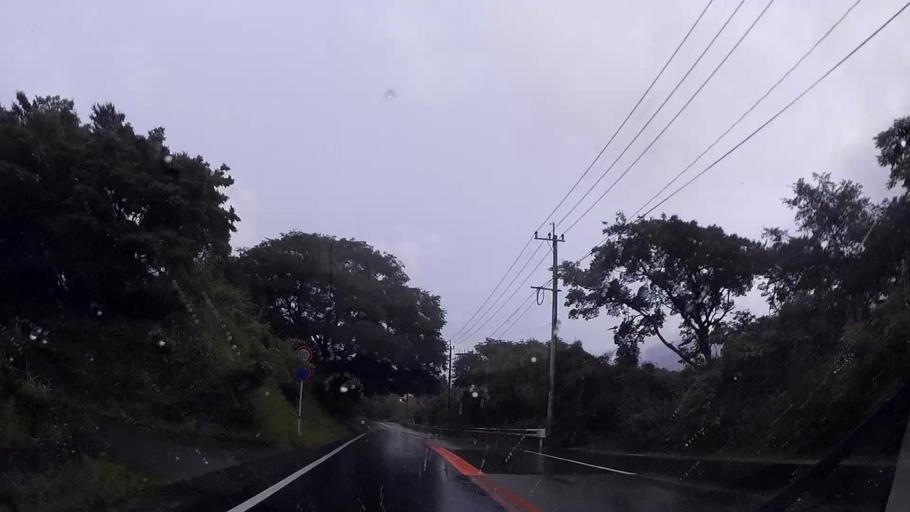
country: JP
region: Kumamoto
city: Aso
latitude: 32.8729
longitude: 130.9930
